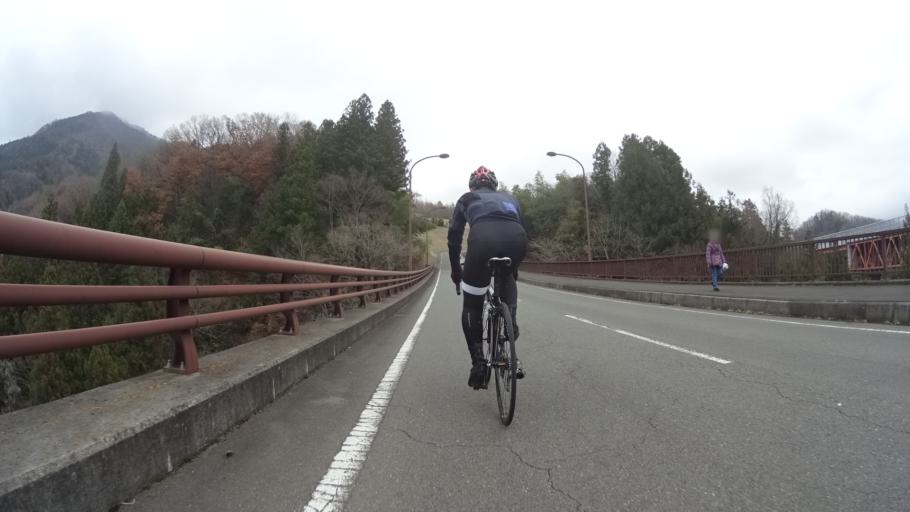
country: JP
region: Yamanashi
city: Otsuki
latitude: 35.6212
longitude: 138.9911
